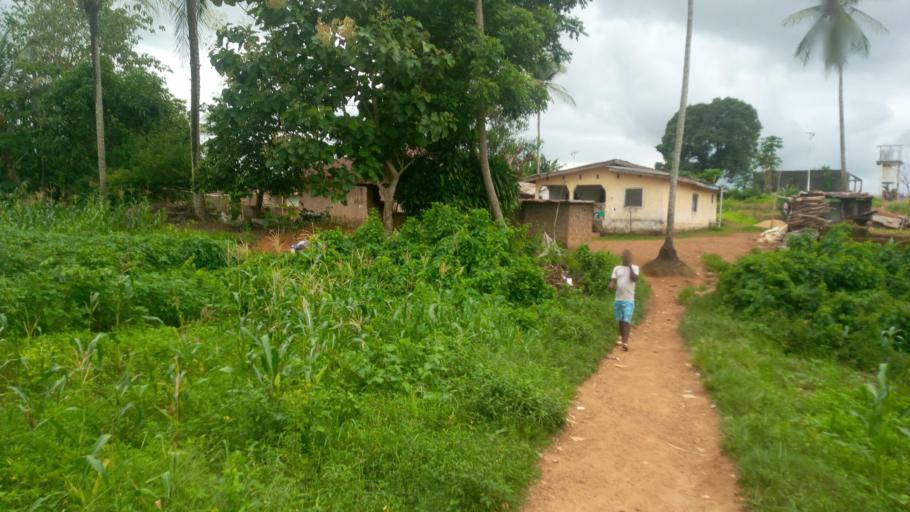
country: SL
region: Southern Province
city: Mogbwemo
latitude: 7.6034
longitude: -12.1793
